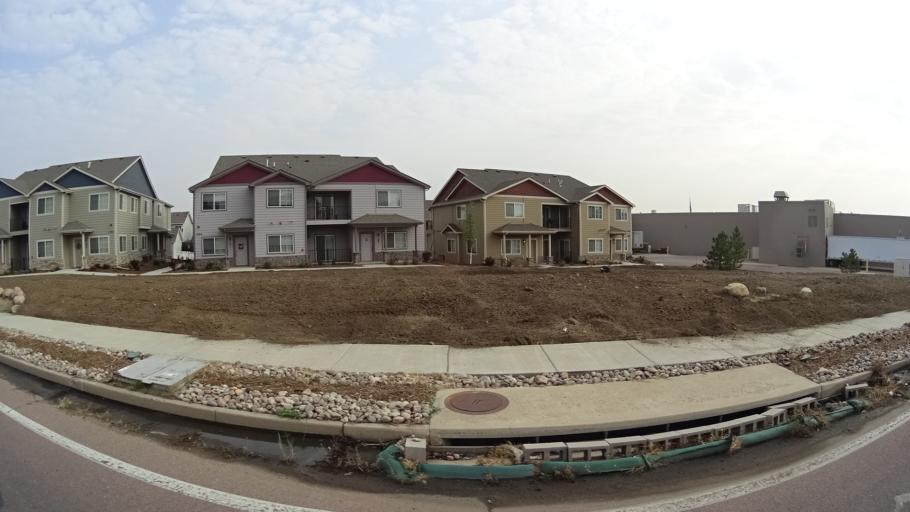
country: US
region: Colorado
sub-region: El Paso County
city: Stratmoor
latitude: 38.8076
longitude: -104.7836
